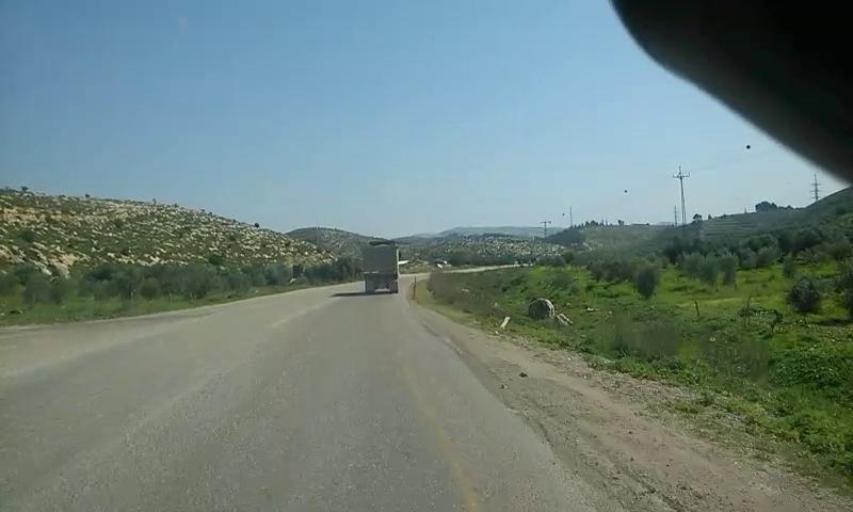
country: PS
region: West Bank
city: Idhna
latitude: 31.5869
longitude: 34.9721
